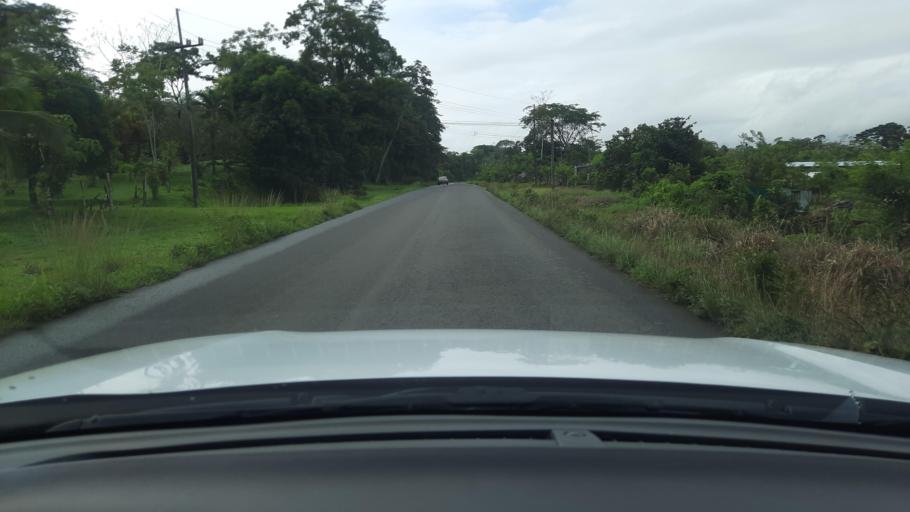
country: CR
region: Alajuela
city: San Jose
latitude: 10.9500
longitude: -85.1226
